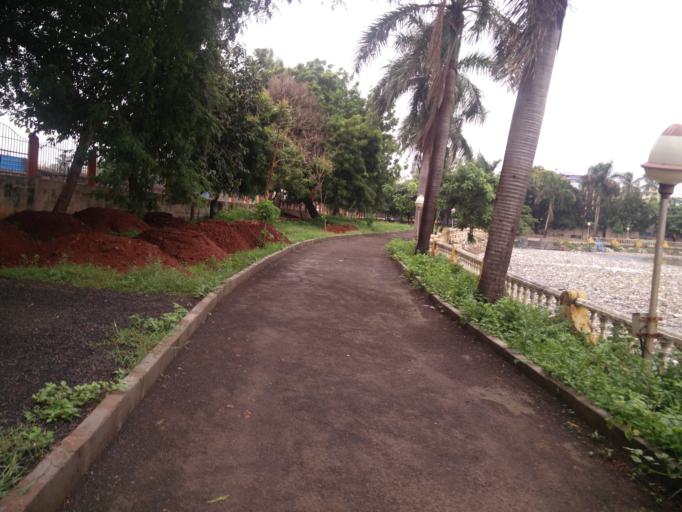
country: IN
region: Andhra Pradesh
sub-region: East Godavari
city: Rajahmundry
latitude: 17.0135
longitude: 81.7800
